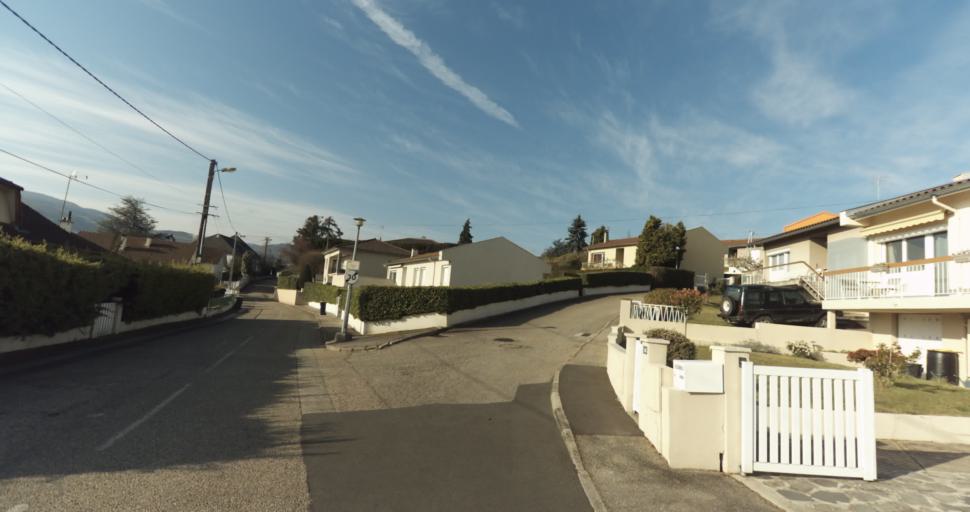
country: FR
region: Rhone-Alpes
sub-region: Departement de la Loire
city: Saint-Jean-Bonnefonds
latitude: 45.4504
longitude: 4.4484
